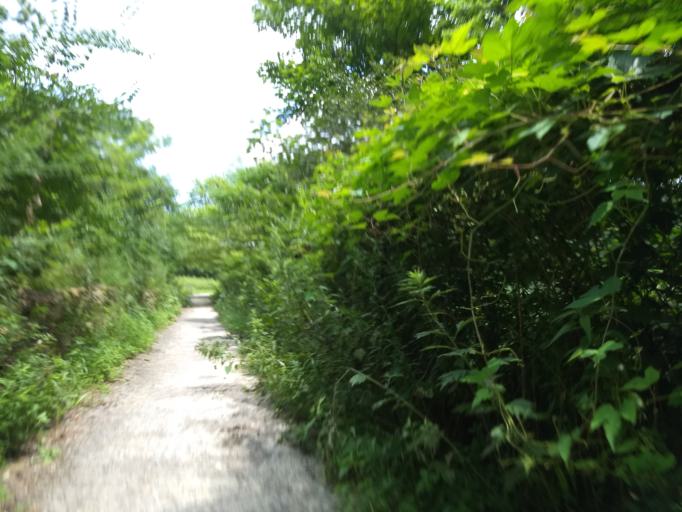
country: US
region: Pennsylvania
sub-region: Allegheny County
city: Homestead
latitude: 40.4193
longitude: -79.9144
